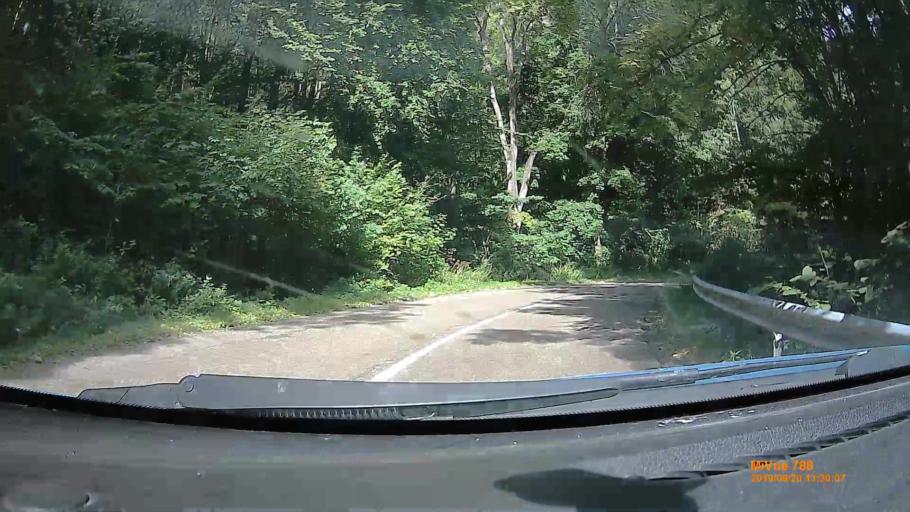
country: HU
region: Heves
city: Szilvasvarad
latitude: 48.0569
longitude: 20.4832
